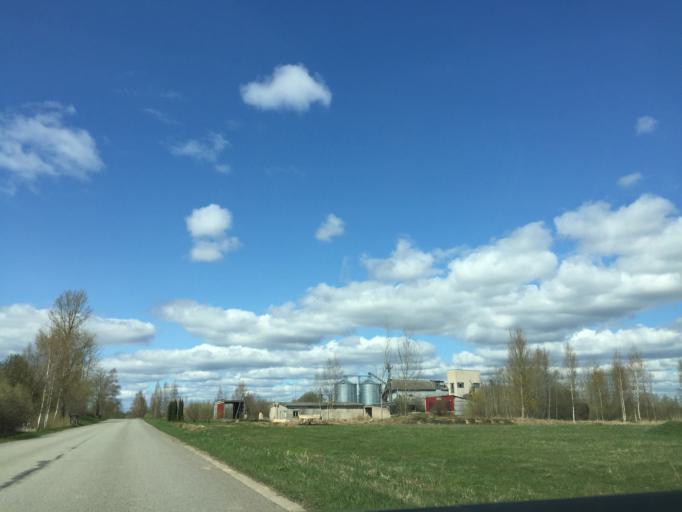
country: LV
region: Vilanu
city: Vilani
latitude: 56.7269
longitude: 27.0792
